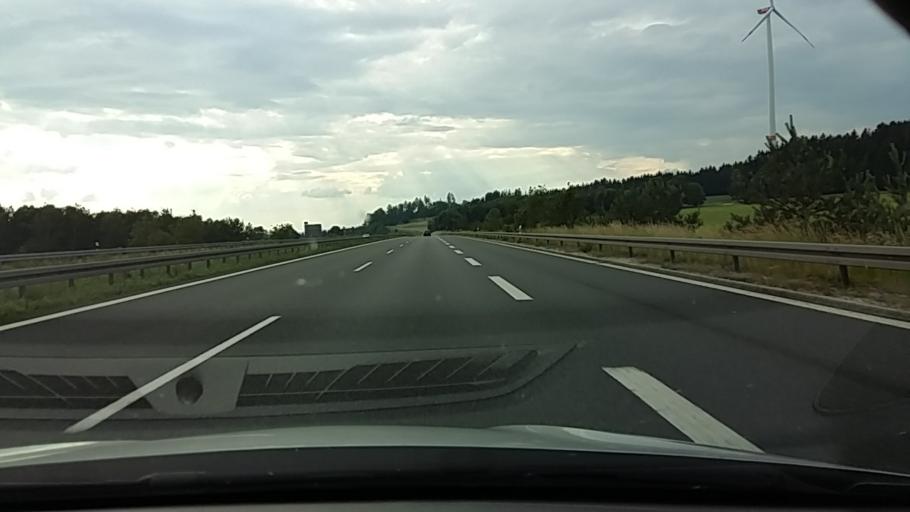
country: DE
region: Bavaria
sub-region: Upper Palatinate
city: Leuchtenberg
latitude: 49.5666
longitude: 12.2385
